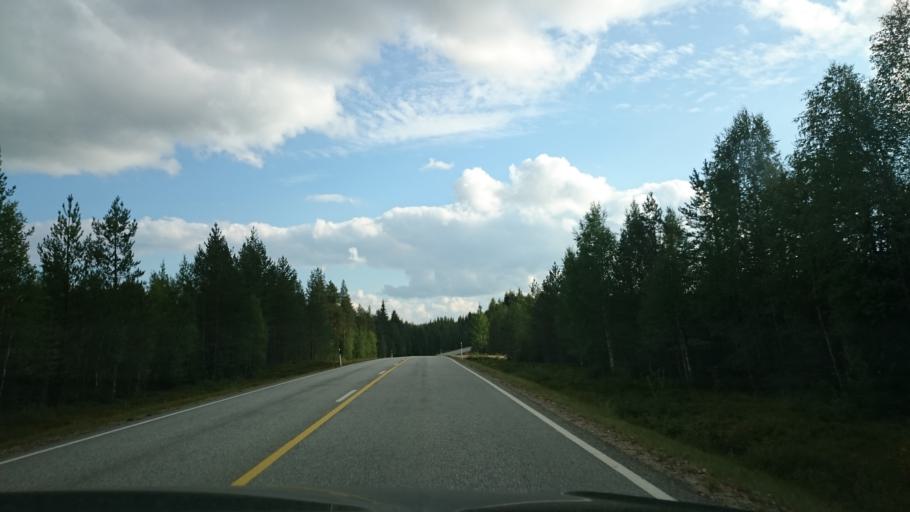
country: FI
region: Kainuu
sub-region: Kehys-Kainuu
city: Kuhmo
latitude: 64.5217
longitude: 29.9461
